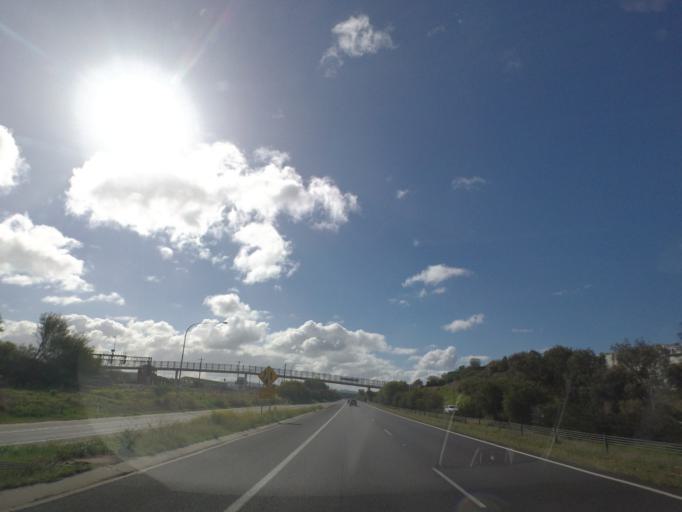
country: AU
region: New South Wales
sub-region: Albury Municipality
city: East Albury
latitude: -36.0891
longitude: 146.9244
